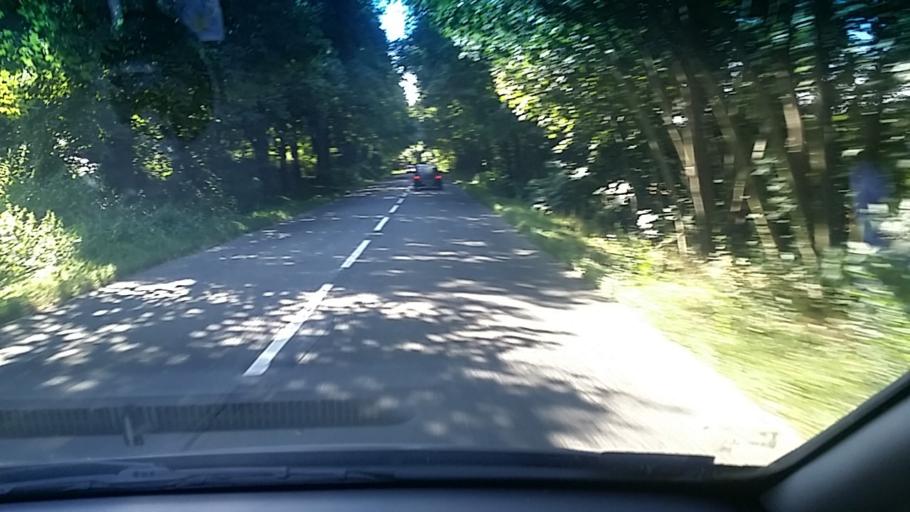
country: HU
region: Nograd
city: Retsag
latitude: 47.9365
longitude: 19.1562
